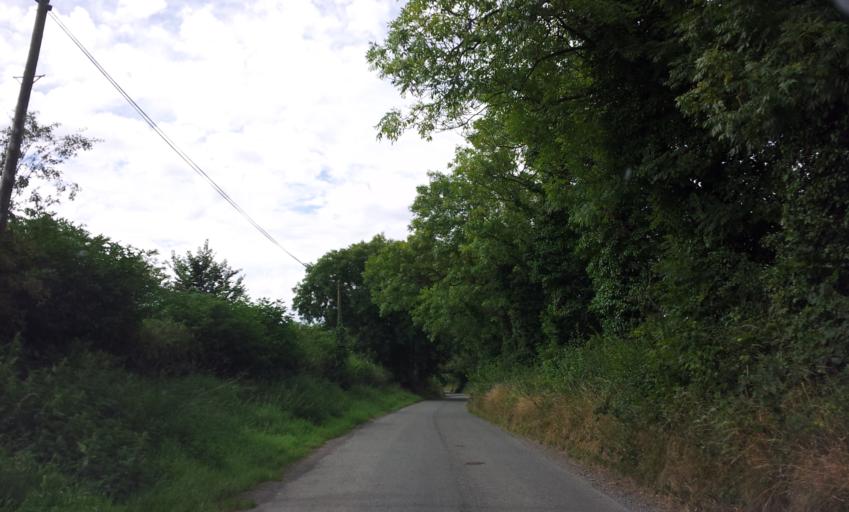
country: IE
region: Leinster
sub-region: Kildare
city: Moone
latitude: 52.9824
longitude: -6.8291
